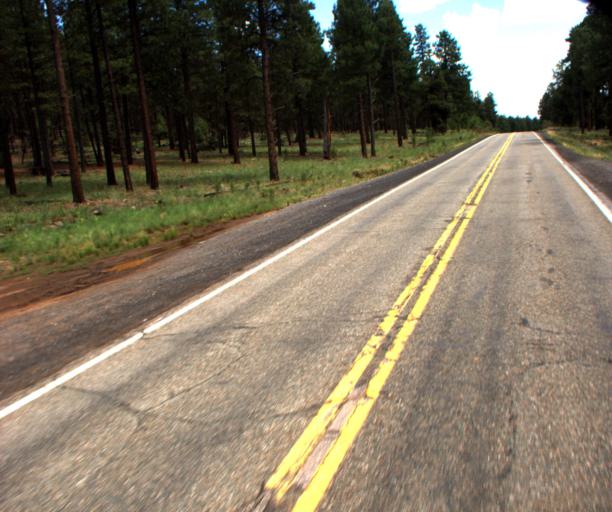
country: US
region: Arizona
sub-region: Coconino County
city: Flagstaff
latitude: 35.3078
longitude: -111.7725
